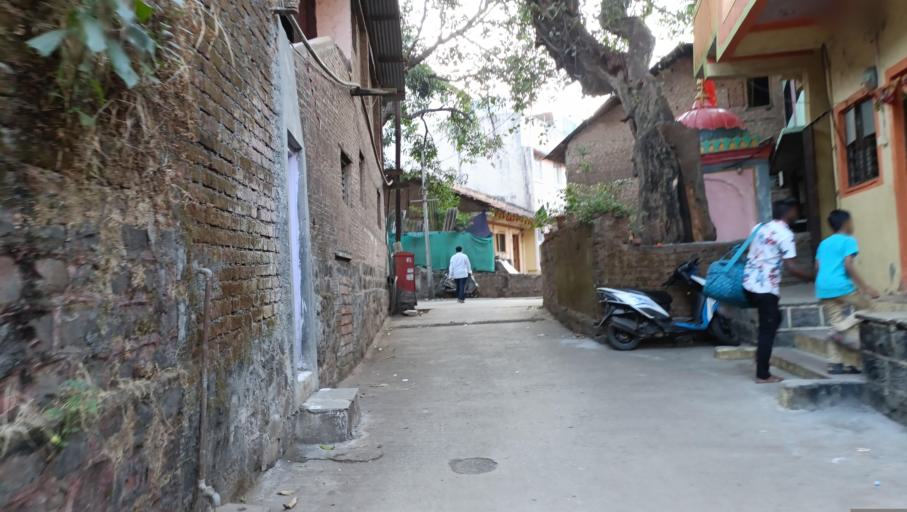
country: IN
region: Maharashtra
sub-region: Nashik Division
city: Trimbak
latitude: 19.9318
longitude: 73.5289
